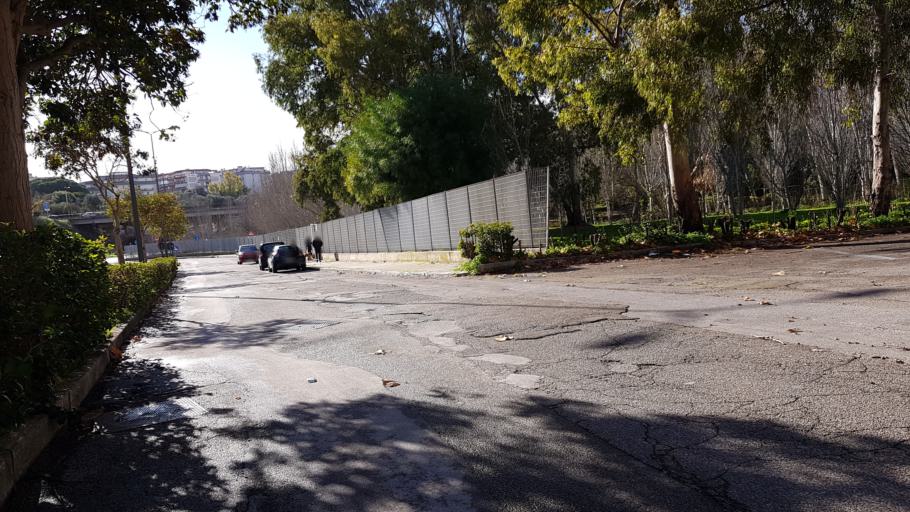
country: IT
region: Apulia
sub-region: Provincia di Brindisi
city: Brindisi
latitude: 40.6296
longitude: 17.9402
